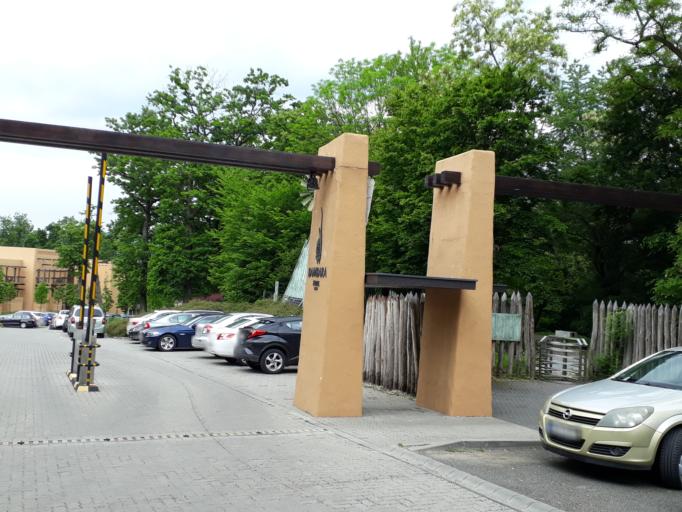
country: HU
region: Heves
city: Felsotarkany
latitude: 47.9773
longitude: 20.4351
